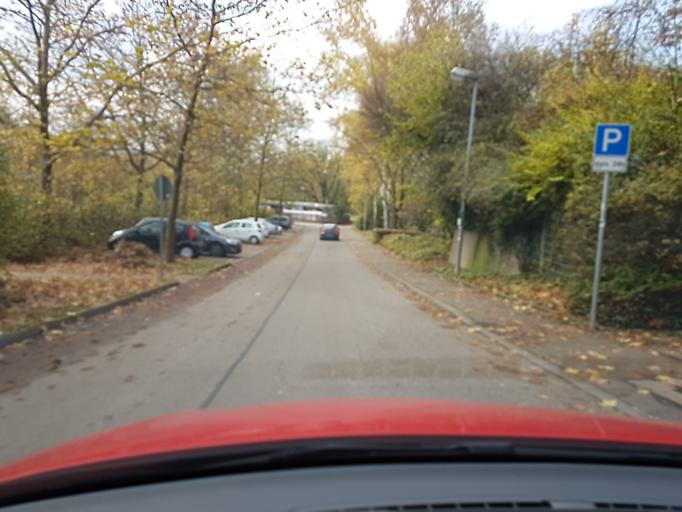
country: DE
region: Baden-Wuerttemberg
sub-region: Regierungsbezirk Stuttgart
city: Neckarsulm
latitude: 49.1883
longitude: 9.2425
